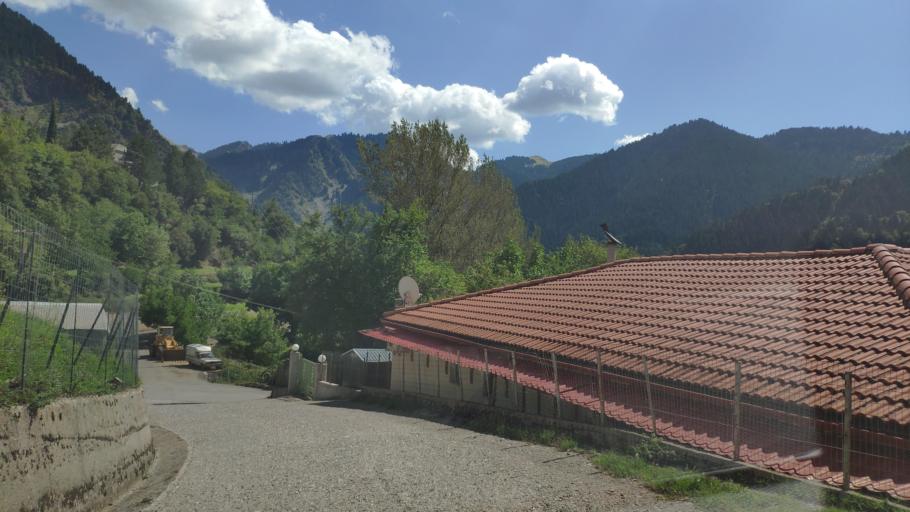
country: GR
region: Central Greece
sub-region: Nomos Evrytanias
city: Kerasochori
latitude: 39.1378
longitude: 21.6473
